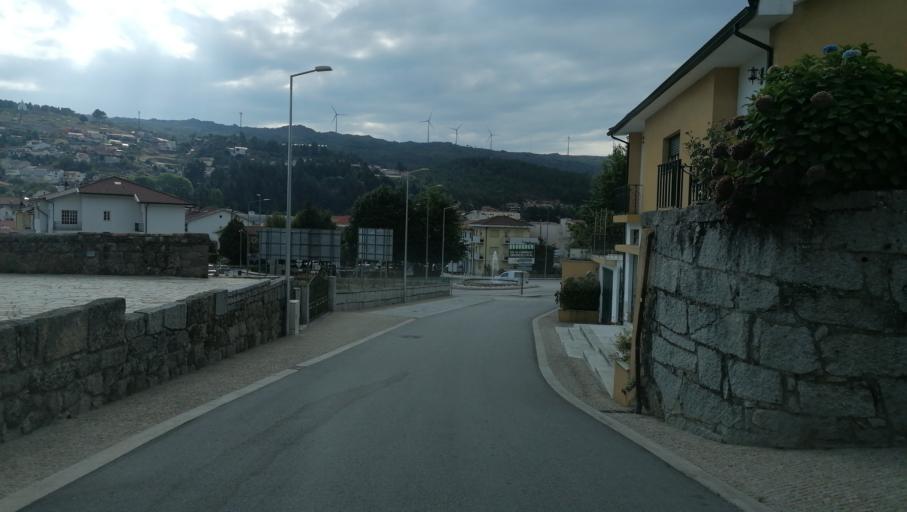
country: PT
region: Vila Real
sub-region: Vila Pouca de Aguiar
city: Vila Pouca de Aguiar
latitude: 41.5018
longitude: -7.6469
